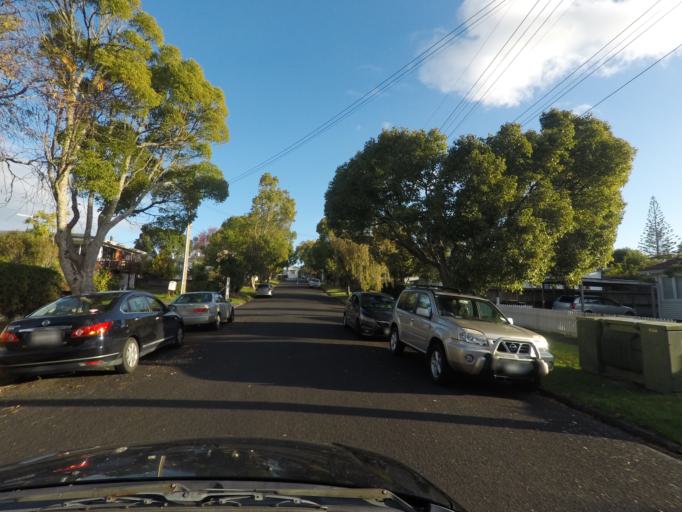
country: NZ
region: Auckland
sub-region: Auckland
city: Waitakere
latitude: -36.9024
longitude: 174.6723
